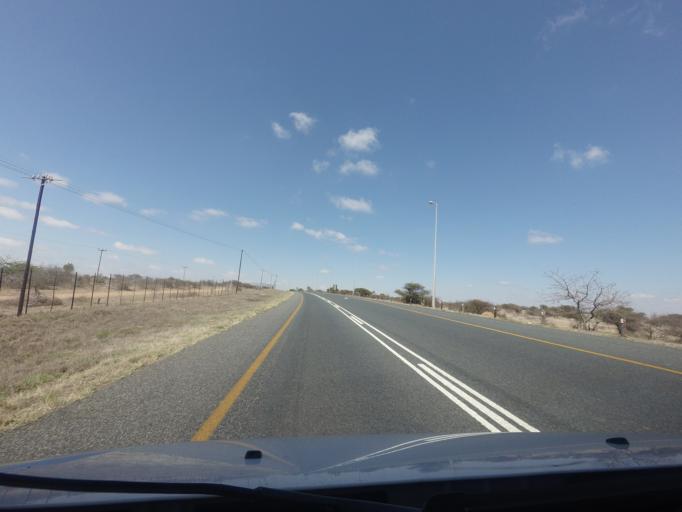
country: ZA
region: Limpopo
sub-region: Vhembe District Municipality
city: Louis Trichardt
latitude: -23.3720
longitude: 29.7708
